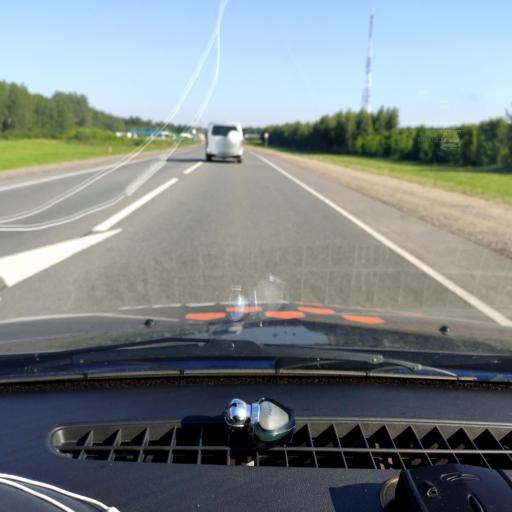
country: RU
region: Orjol
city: Orel
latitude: 52.9194
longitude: 36.1498
